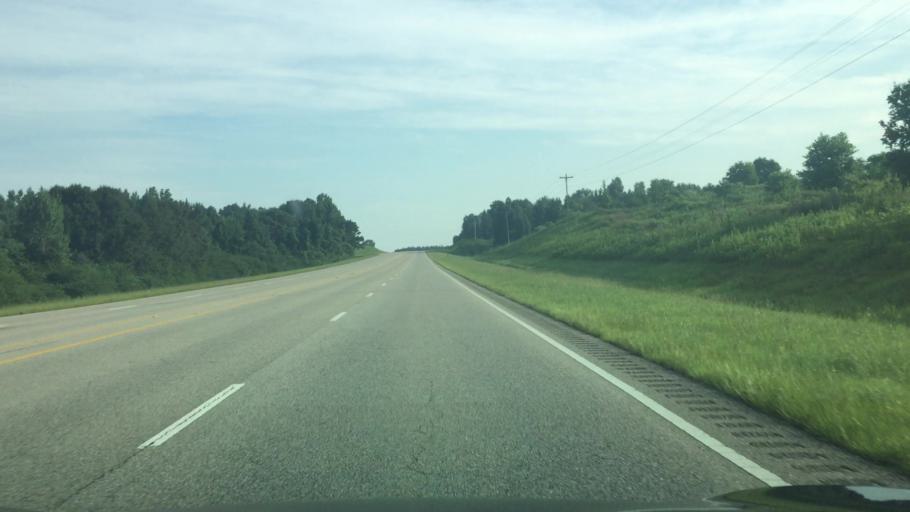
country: US
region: Alabama
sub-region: Covington County
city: Andalusia
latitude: 31.4307
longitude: -86.6116
